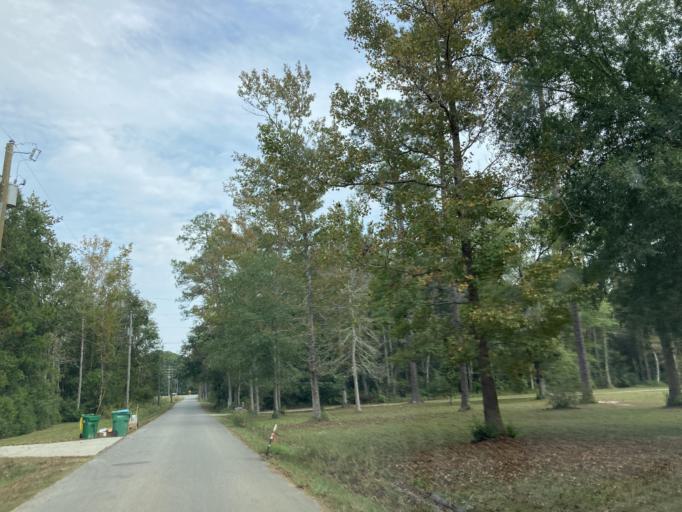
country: US
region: Mississippi
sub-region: Jackson County
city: Saint Martin
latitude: 30.4666
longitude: -88.8504
